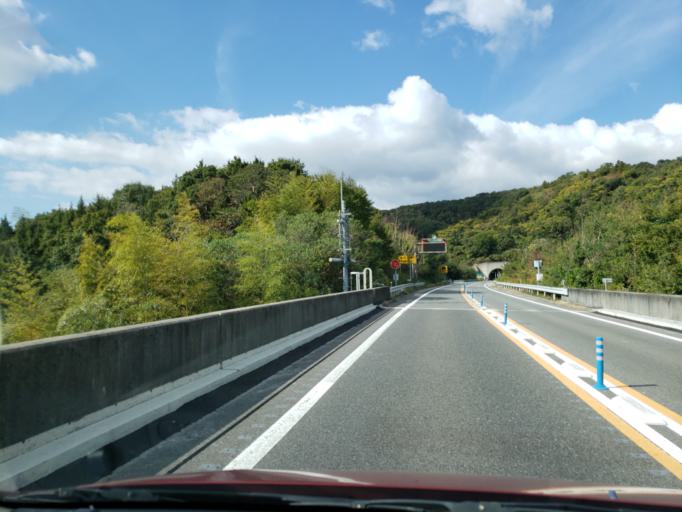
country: JP
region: Tokushima
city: Kamojimacho-jogejima
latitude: 34.1045
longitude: 134.2973
